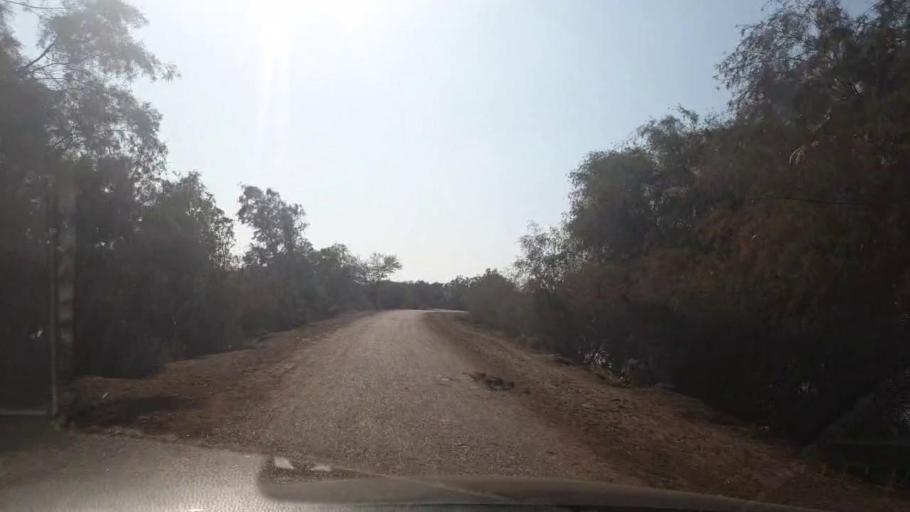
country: PK
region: Sindh
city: Khairpur
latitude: 28.1386
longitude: 69.6010
